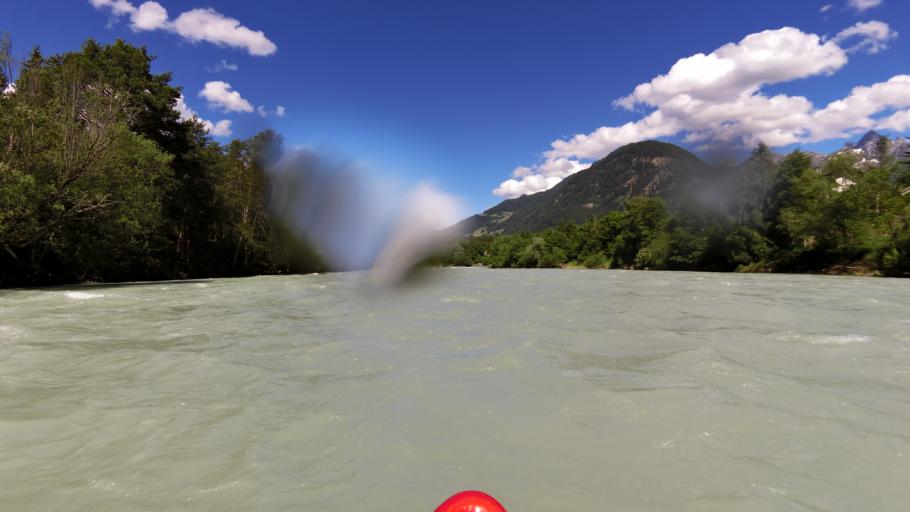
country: AT
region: Tyrol
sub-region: Politischer Bezirk Imst
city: Roppen
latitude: 47.2274
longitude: 10.8315
